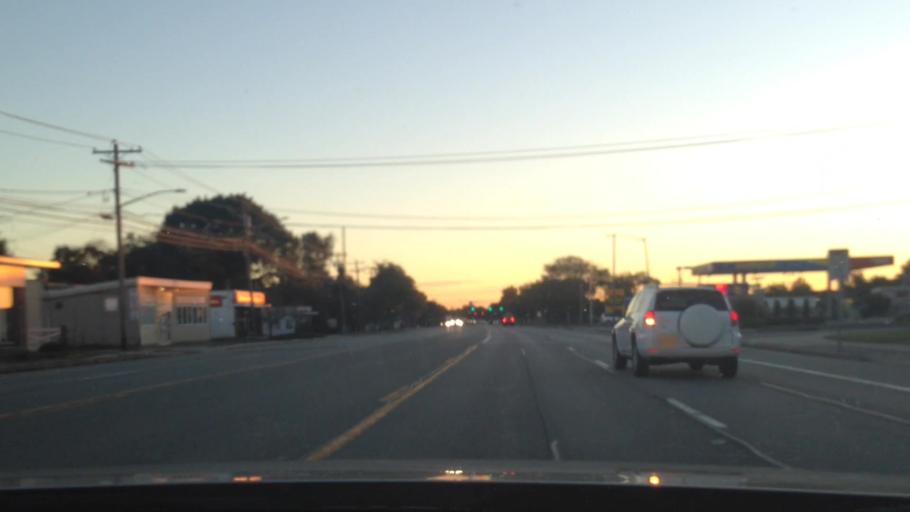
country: US
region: New York
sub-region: Suffolk County
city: Mount Sinai
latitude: 40.9360
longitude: -73.0171
